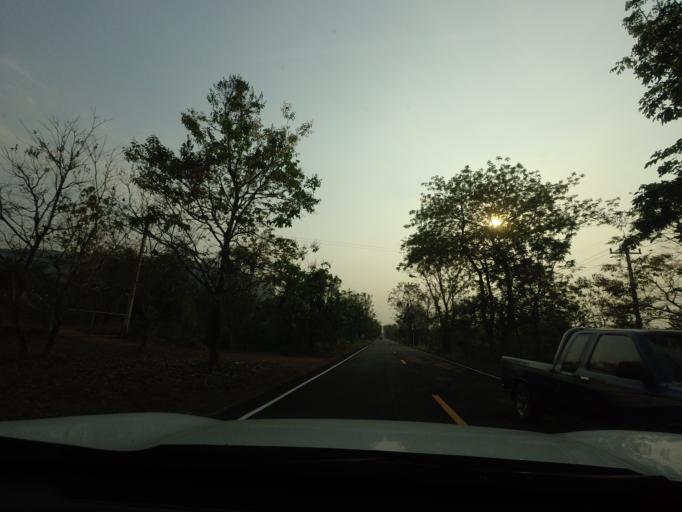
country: TH
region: Nakhon Nayok
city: Pak Phli
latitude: 14.1973
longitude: 101.3860
